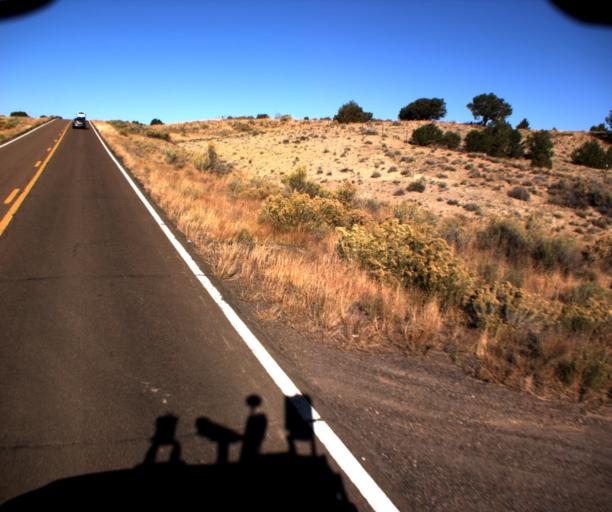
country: US
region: Arizona
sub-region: Apache County
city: Ganado
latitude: 35.7509
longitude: -109.8826
